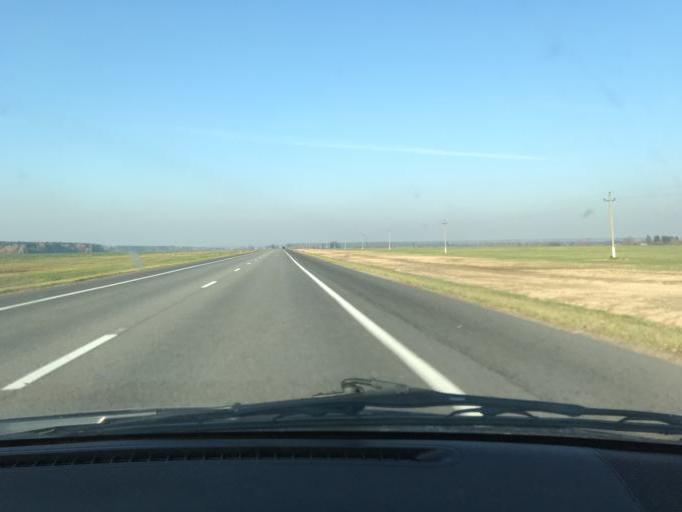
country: BY
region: Vitebsk
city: Orsha
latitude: 54.3564
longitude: 30.4452
